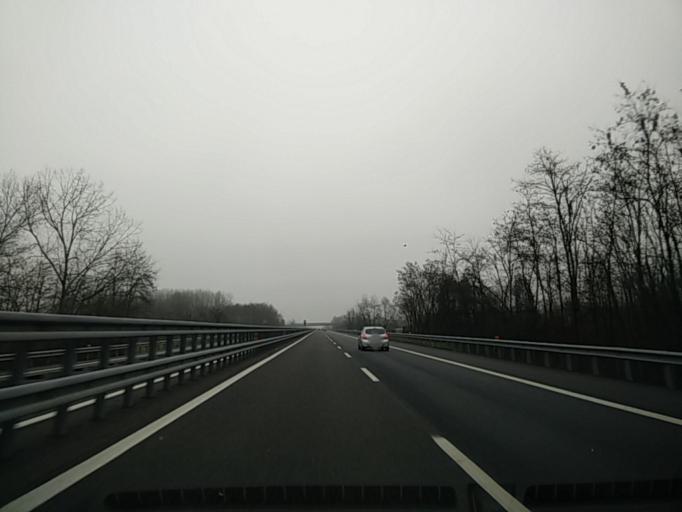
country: IT
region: Piedmont
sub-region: Provincia di Asti
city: Villafranca d'Asti
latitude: 44.9257
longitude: 8.0140
